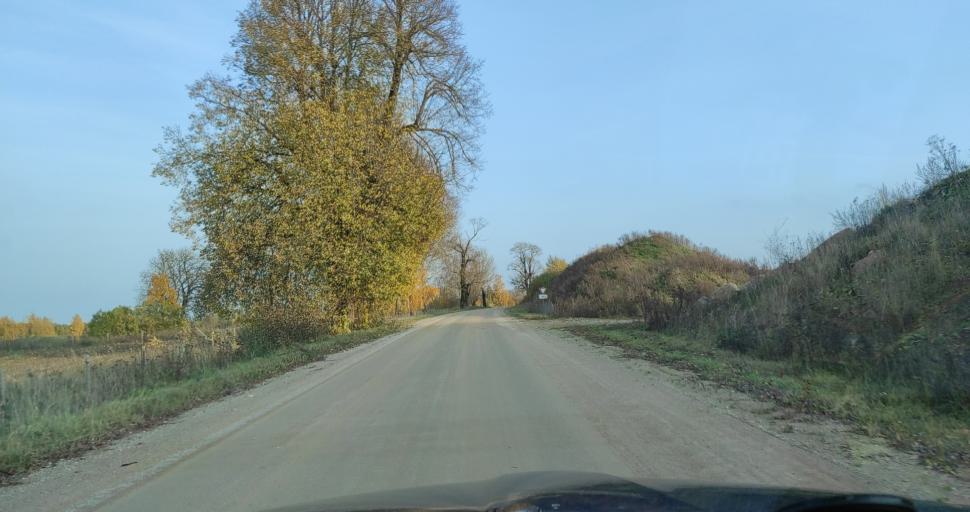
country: LV
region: Vainode
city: Vainode
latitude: 56.4429
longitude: 21.8677
